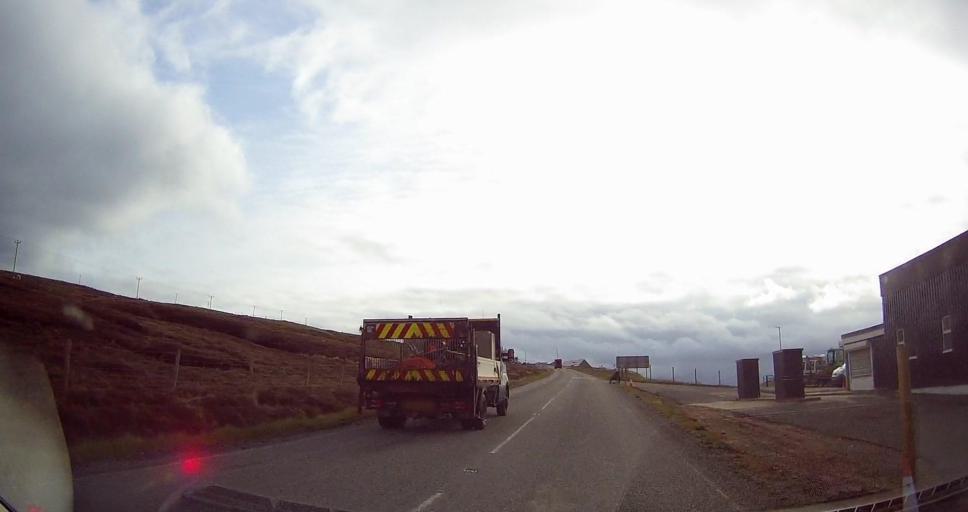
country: GB
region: Scotland
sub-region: Shetland Islands
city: Lerwick
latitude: 60.4451
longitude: -1.2102
